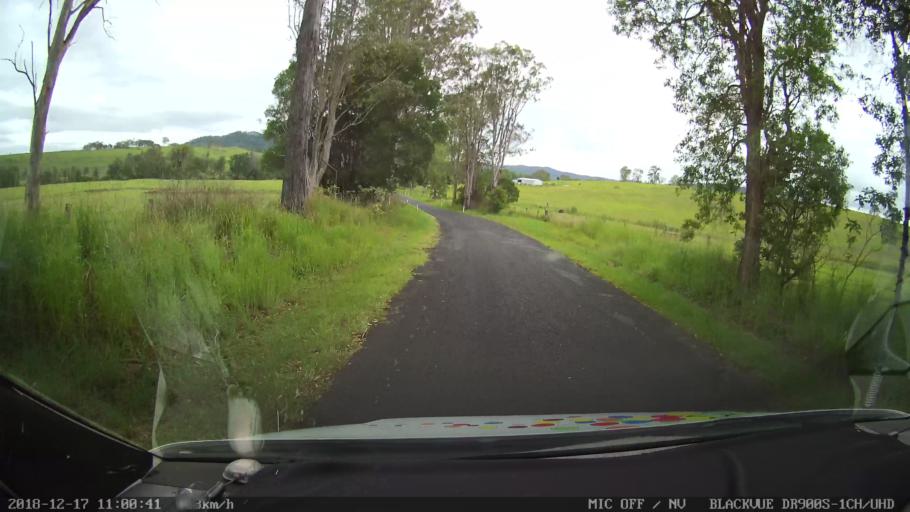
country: AU
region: New South Wales
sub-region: Richmond Valley
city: Casino
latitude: -28.8188
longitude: 152.6204
